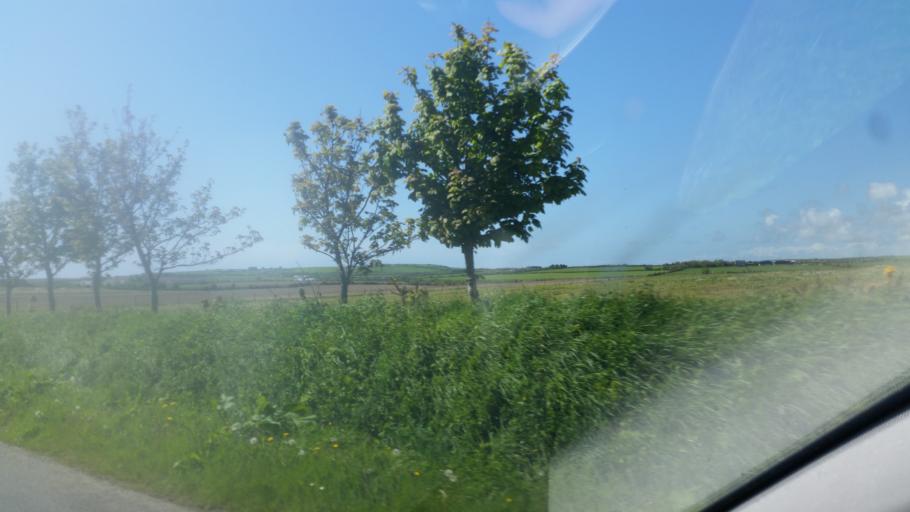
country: IE
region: Munster
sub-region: Waterford
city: Dunmore East
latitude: 52.1933
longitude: -6.8553
